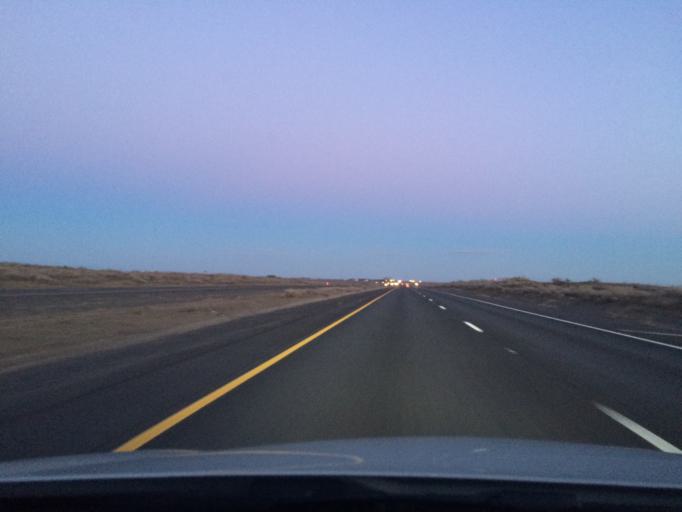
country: US
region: Washington
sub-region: Grant County
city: Royal City
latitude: 47.1037
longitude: -119.6550
